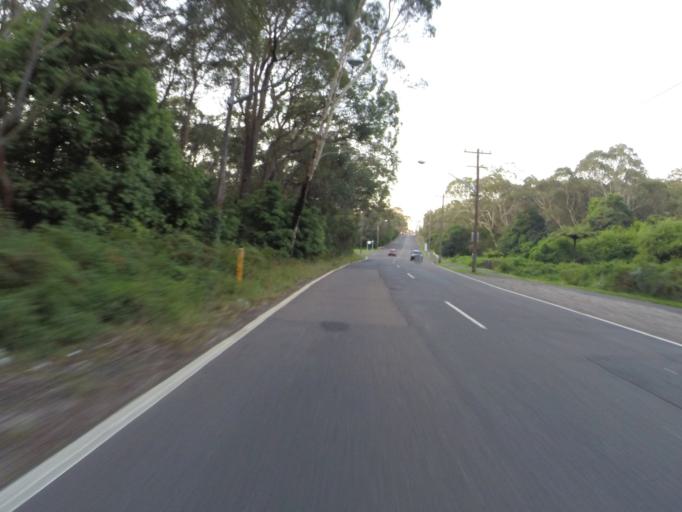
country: AU
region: New South Wales
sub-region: Bankstown
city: Revesby
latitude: -33.9697
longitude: 151.0150
